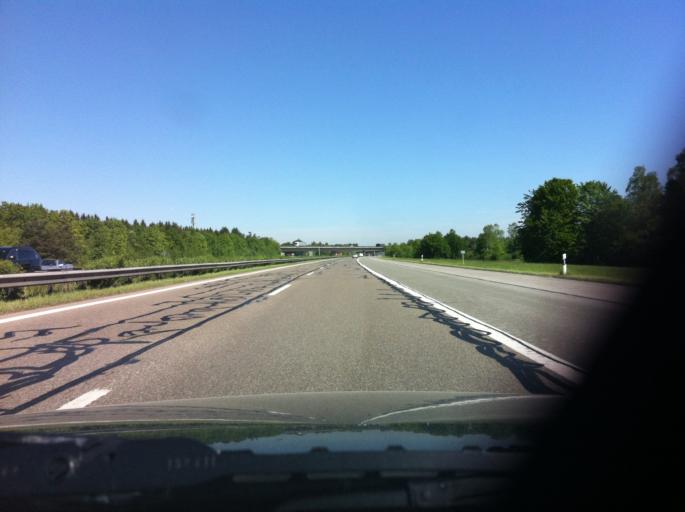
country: DE
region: Bavaria
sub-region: Upper Bavaria
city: Brunnthal
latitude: 48.0187
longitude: 11.6621
